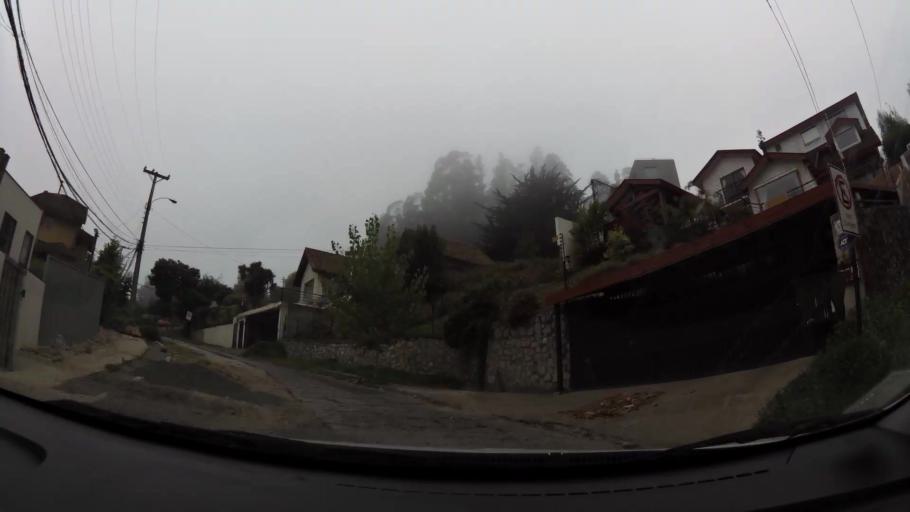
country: CL
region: Biobio
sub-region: Provincia de Concepcion
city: Concepcion
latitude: -36.8262
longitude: -73.0295
